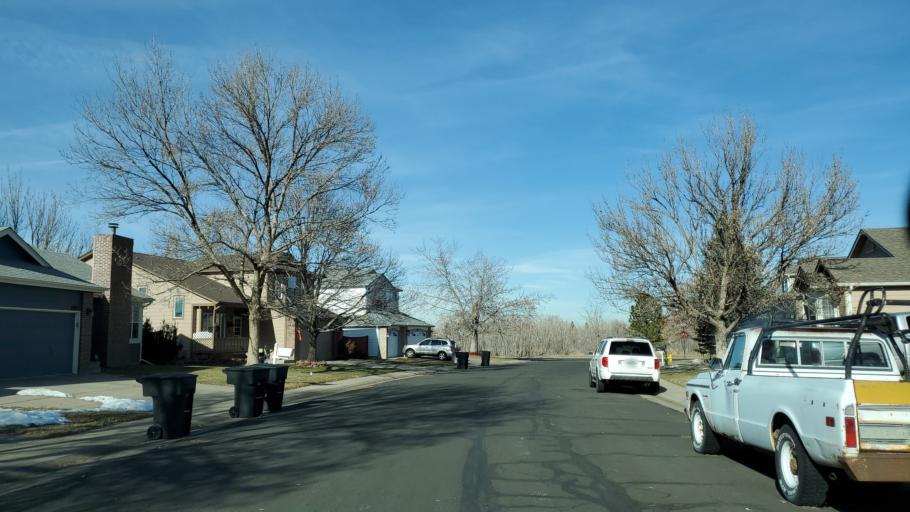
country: US
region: Colorado
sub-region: Adams County
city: Northglenn
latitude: 39.9161
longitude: -104.9550
